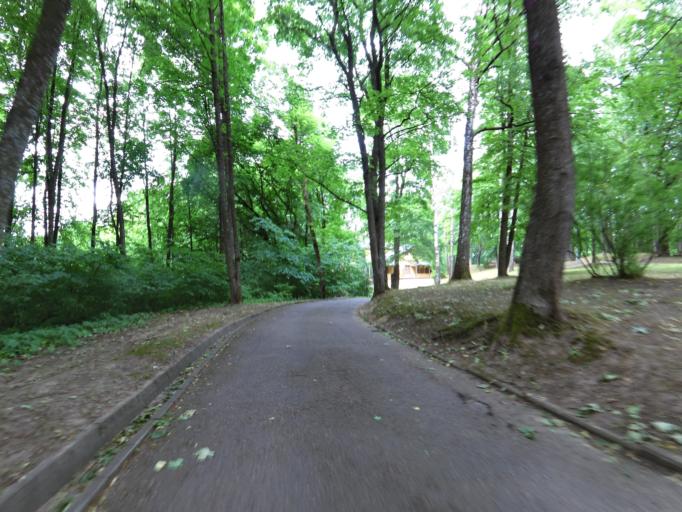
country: LT
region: Vilnius County
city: Rasos
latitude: 54.6733
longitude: 25.3246
